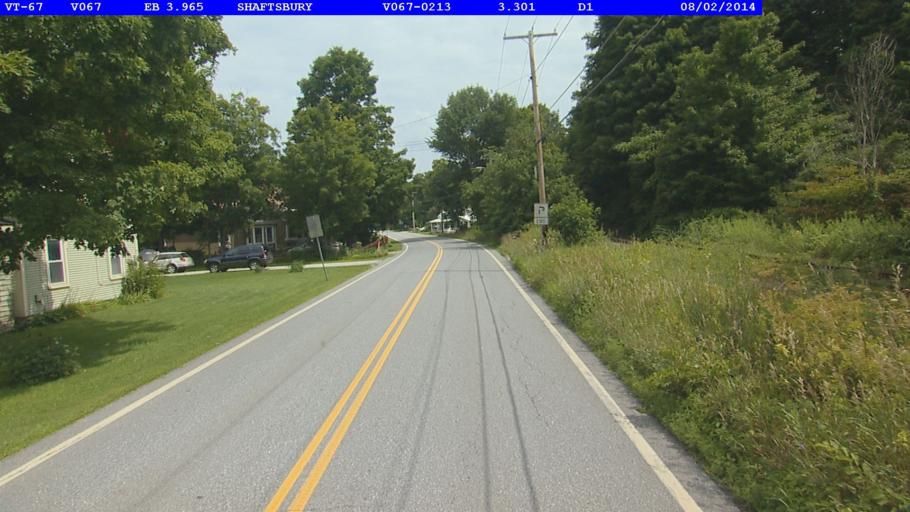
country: US
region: Vermont
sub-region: Bennington County
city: North Bennington
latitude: 42.9469
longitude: -73.2154
